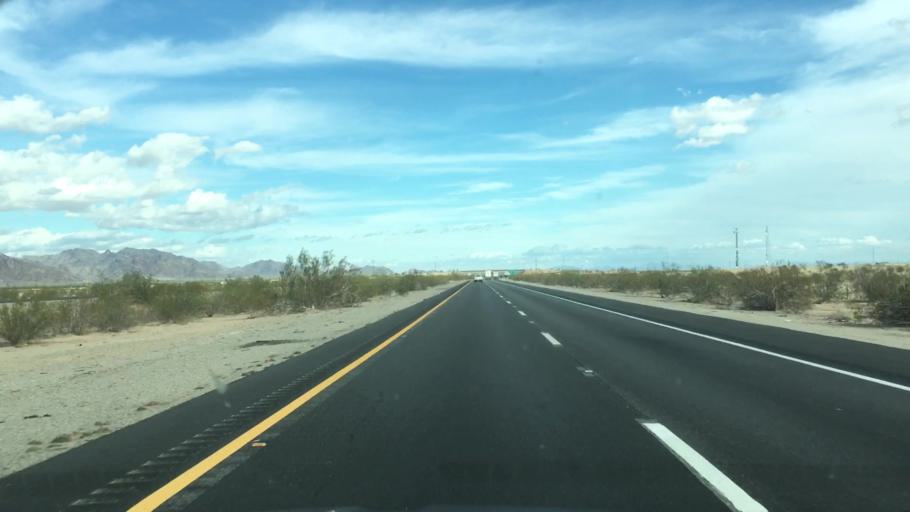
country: US
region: California
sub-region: Riverside County
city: Mesa Verde
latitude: 33.6070
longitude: -114.9127
